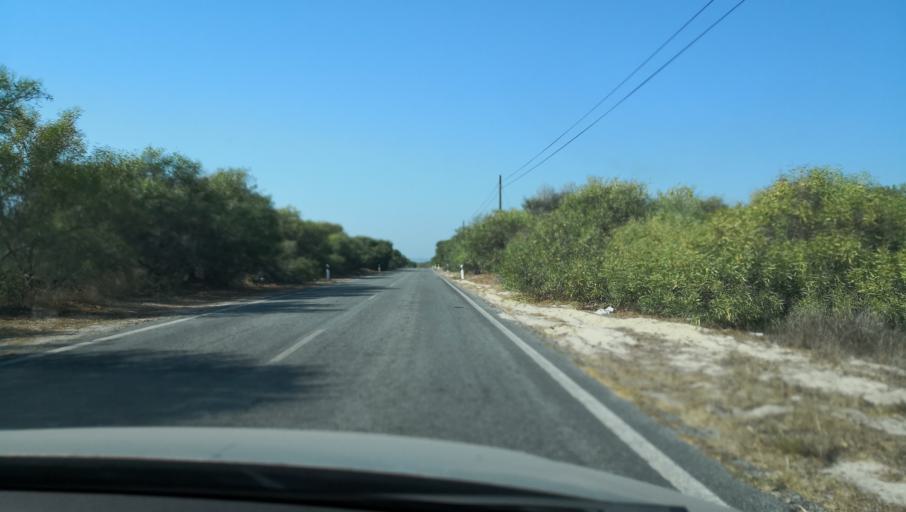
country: PT
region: Setubal
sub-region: Setubal
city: Setubal
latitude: 38.4038
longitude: -8.8081
